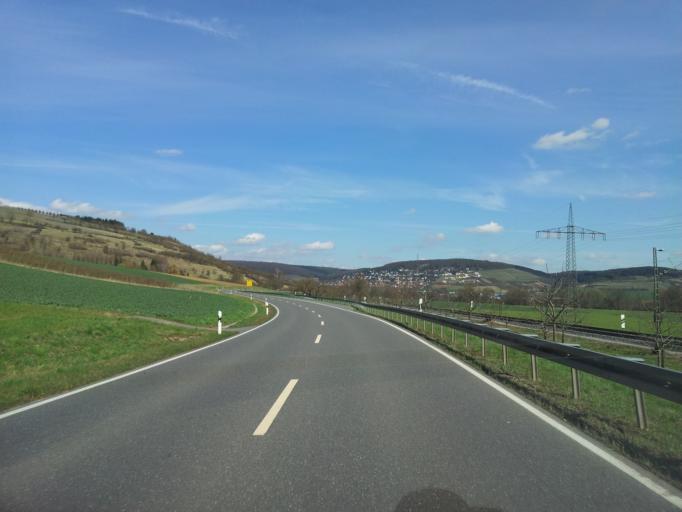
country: DE
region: Baden-Wuerttemberg
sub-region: Regierungsbezirk Stuttgart
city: Lauda-Konigshofen
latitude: 49.5323
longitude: 9.7126
